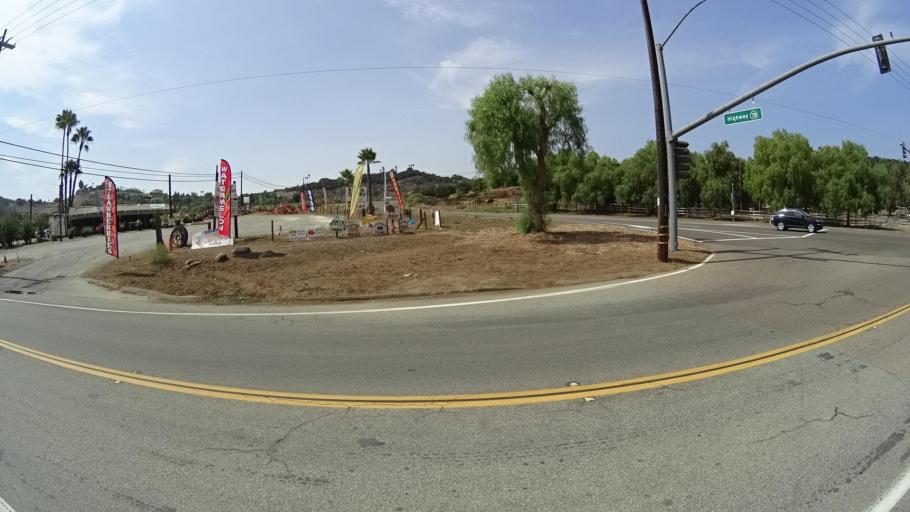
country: US
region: California
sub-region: San Diego County
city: San Pasqual
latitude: 33.0974
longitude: -117.0209
